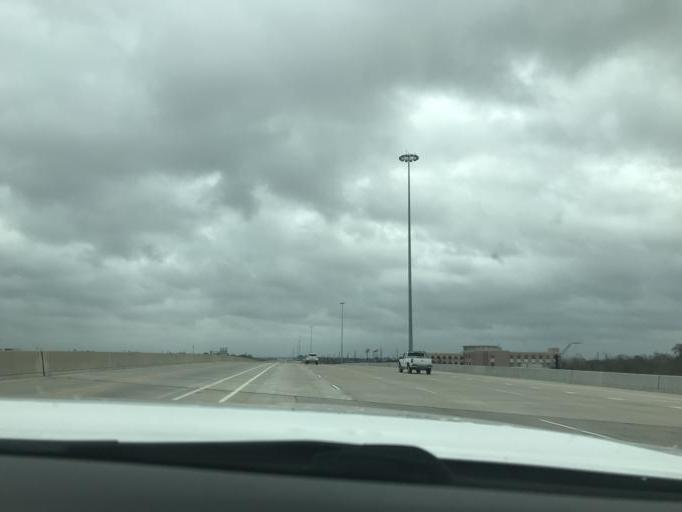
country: US
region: Texas
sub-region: Fort Bend County
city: Greatwood
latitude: 29.5558
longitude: -95.7178
